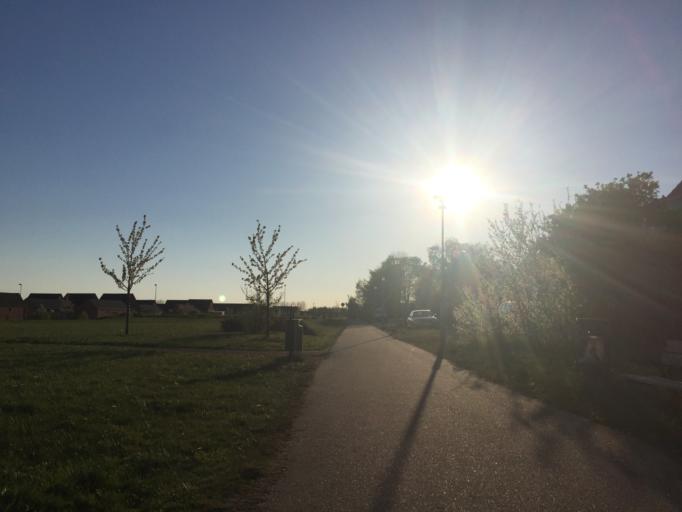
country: SE
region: Skane
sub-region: Malmo
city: Bunkeflostrand
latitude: 55.5533
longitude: 12.9646
